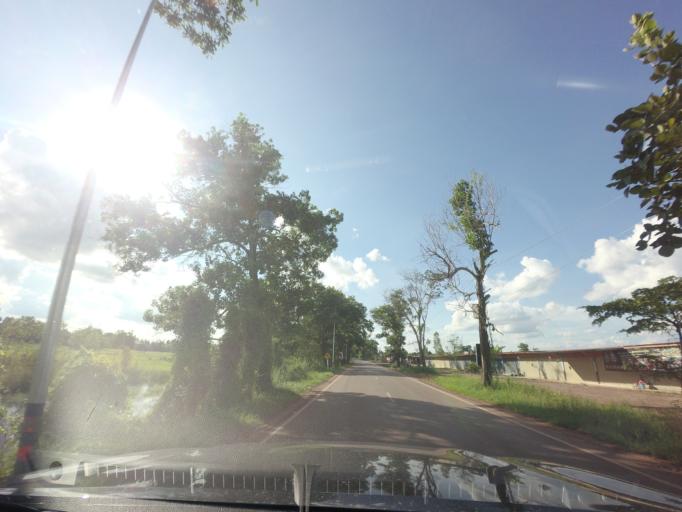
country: TH
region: Changwat Udon Thani
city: Ban Dung
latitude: 17.7409
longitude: 103.3433
